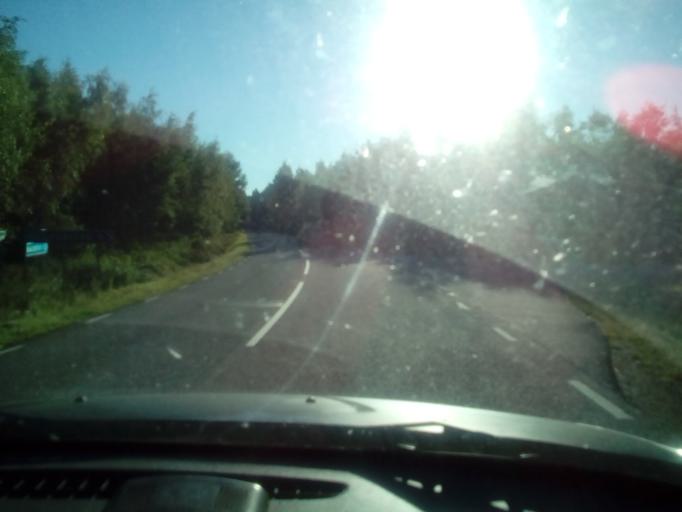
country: SE
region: Kalmar
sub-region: Vasterviks Kommun
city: Ankarsrum
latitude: 57.7961
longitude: 16.3637
